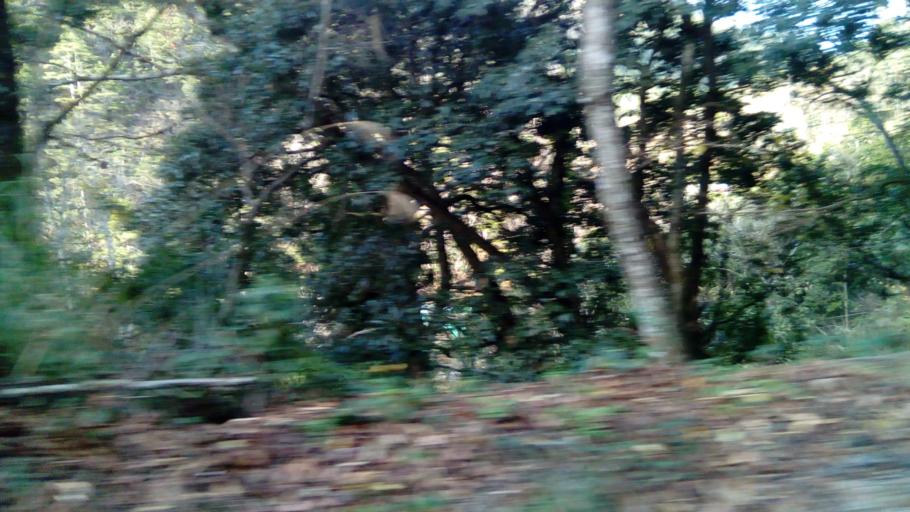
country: TW
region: Taiwan
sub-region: Hualien
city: Hualian
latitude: 24.3435
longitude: 121.3135
